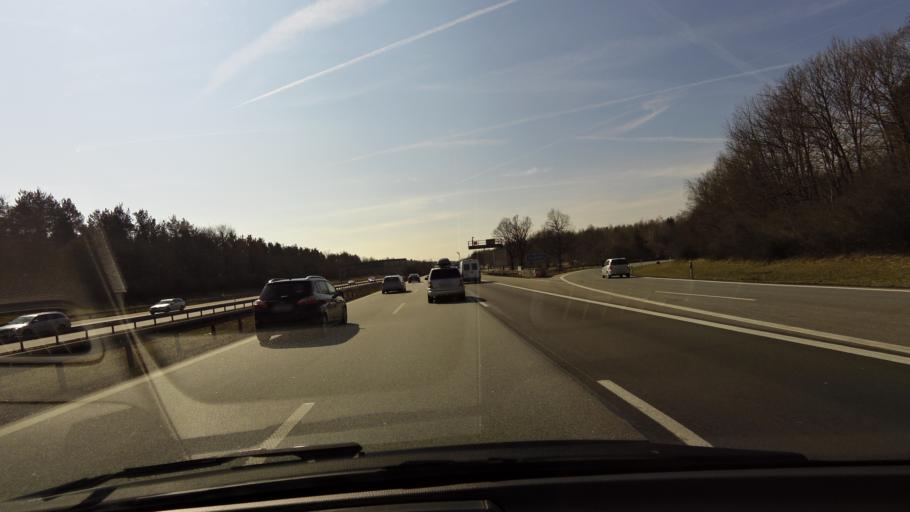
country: DE
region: Bavaria
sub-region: Upper Bavaria
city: Vaterstetten
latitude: 48.1104
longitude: 11.7555
